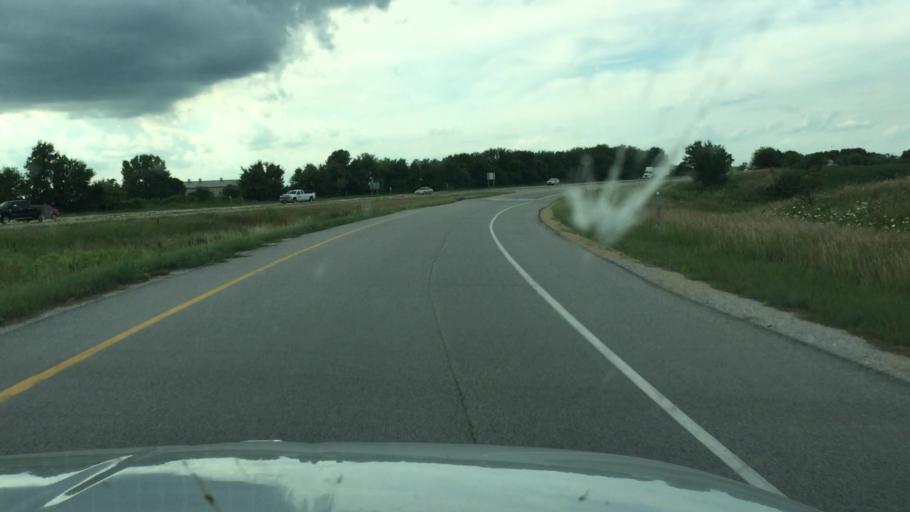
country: US
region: Iowa
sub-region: Scott County
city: Blue Grass
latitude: 41.5407
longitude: -90.6767
